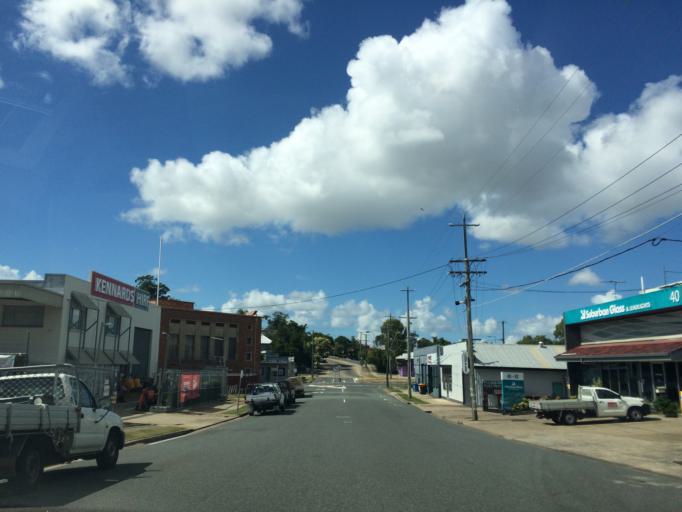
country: AU
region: Queensland
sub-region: Brisbane
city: Woolloongabba
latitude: -27.4888
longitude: 153.0498
